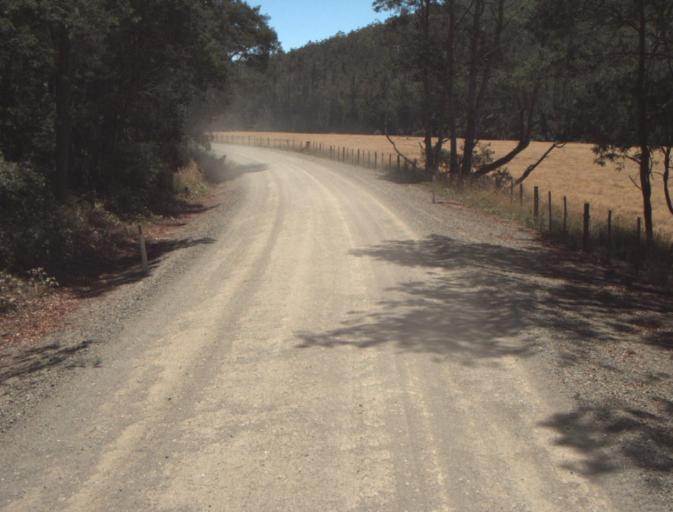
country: AU
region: Tasmania
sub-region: Dorset
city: Scottsdale
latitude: -41.2909
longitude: 147.3927
